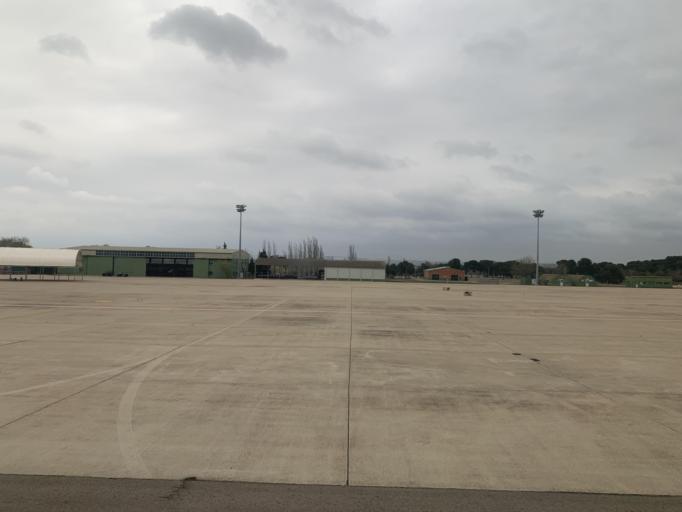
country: ES
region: Aragon
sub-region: Provincia de Zaragoza
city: Utebo
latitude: 41.6703
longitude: -1.0359
